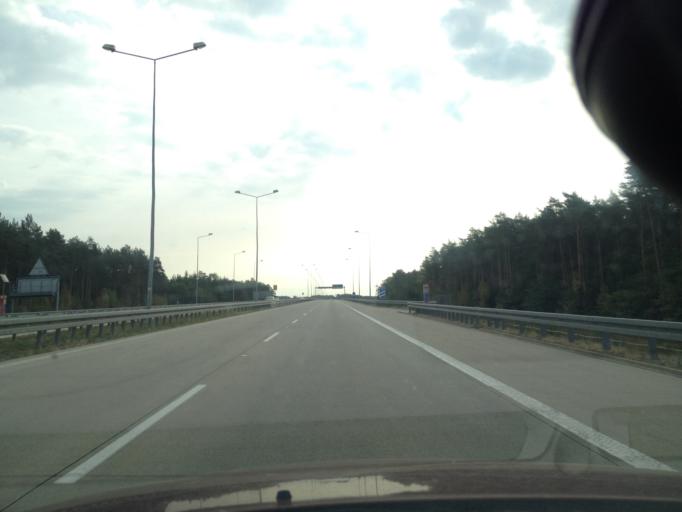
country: PL
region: Lower Silesian Voivodeship
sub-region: Powiat zgorzelecki
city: Wegliniec
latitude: 51.2166
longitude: 15.2303
